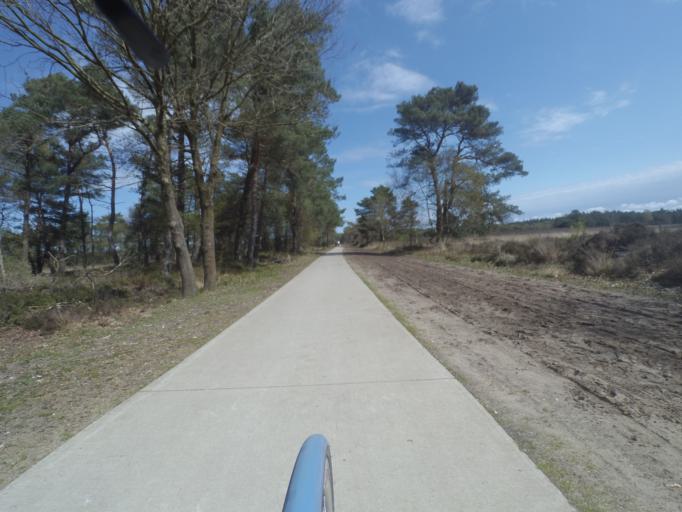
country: NL
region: Gelderland
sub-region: Gemeente Epe
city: Emst
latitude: 52.3355
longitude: 5.9042
